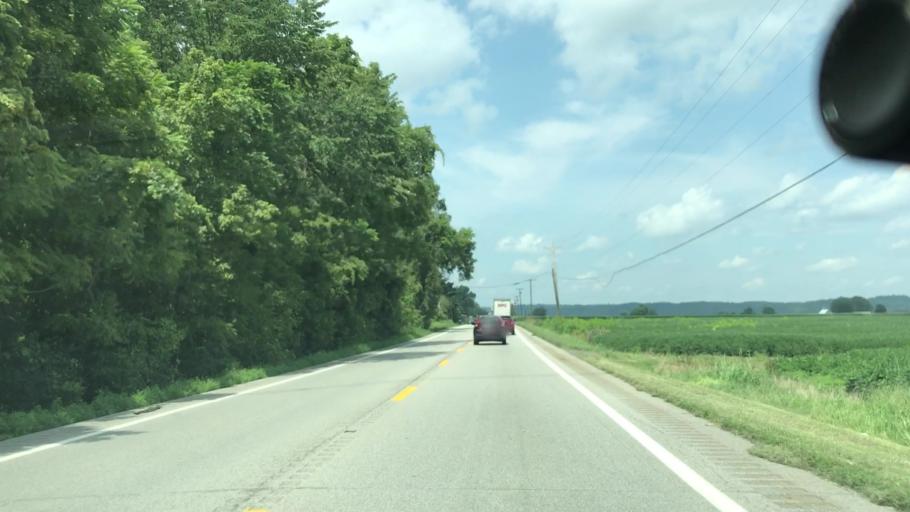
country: US
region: West Virginia
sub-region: Putnam County
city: Buffalo
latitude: 38.7424
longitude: -81.9790
